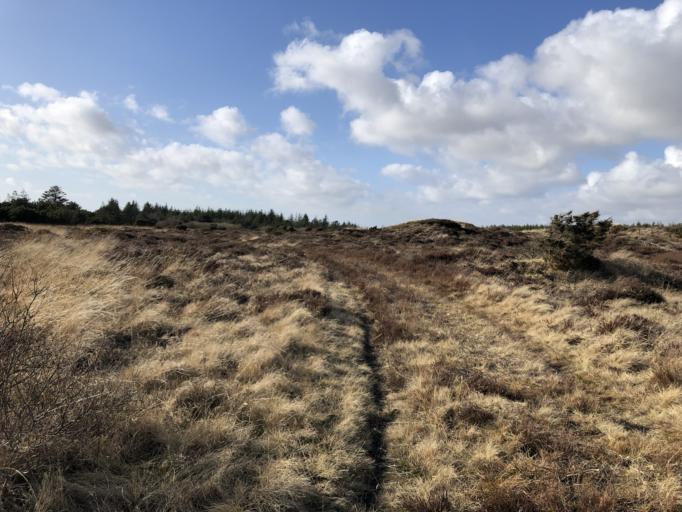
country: DK
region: Central Jutland
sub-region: Holstebro Kommune
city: Ulfborg
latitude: 56.2722
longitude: 8.3554
